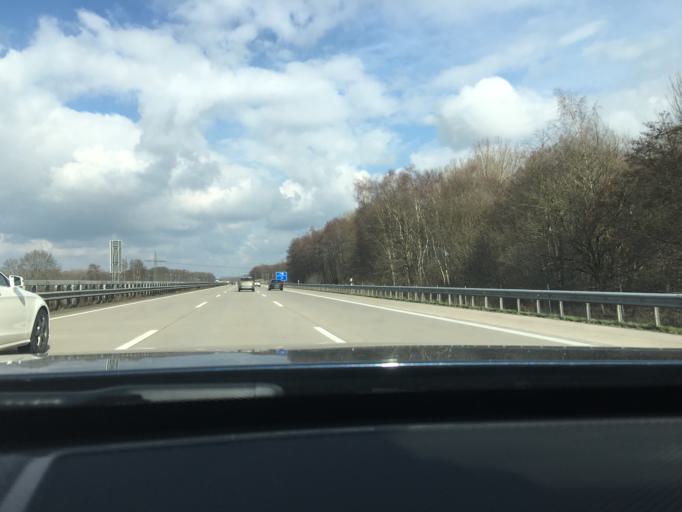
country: DE
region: Lower Saxony
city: Bakum
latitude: 52.7766
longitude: 8.1957
